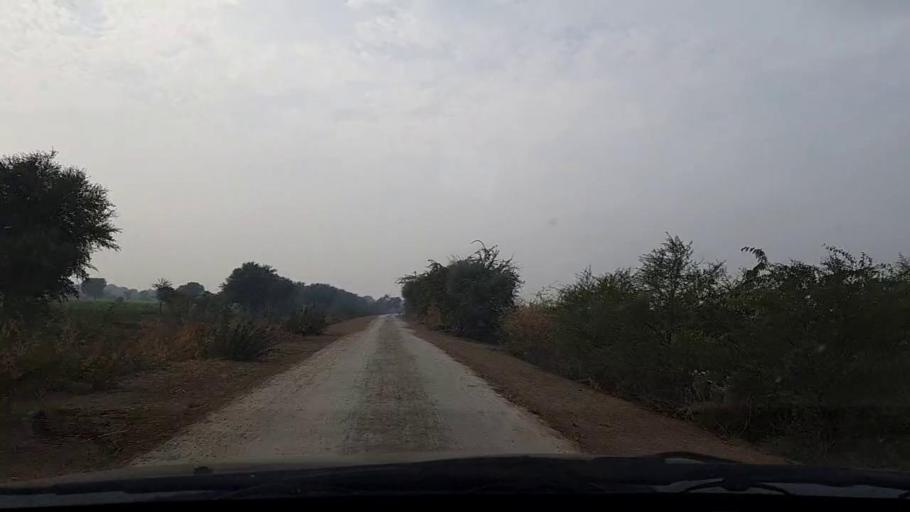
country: PK
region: Sindh
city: Pithoro
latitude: 25.7100
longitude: 69.3914
